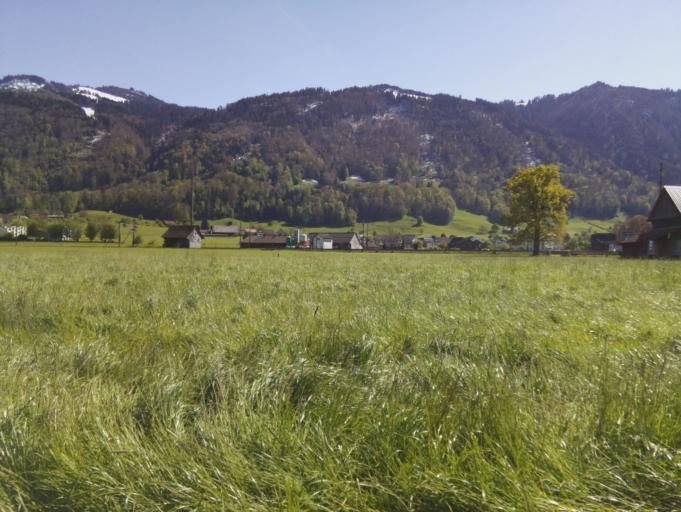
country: CH
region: Schwyz
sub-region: Bezirk March
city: Schubelbach
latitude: 47.1780
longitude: 8.9310
